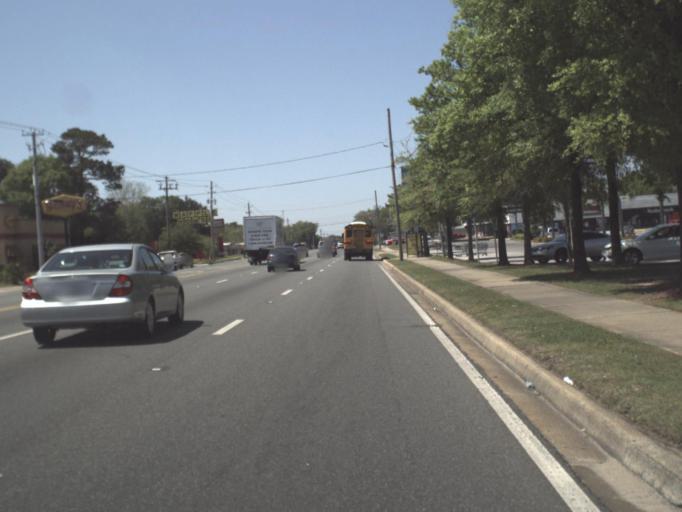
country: US
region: Florida
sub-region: Escambia County
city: West Pensacola
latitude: 30.4367
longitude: -87.2784
